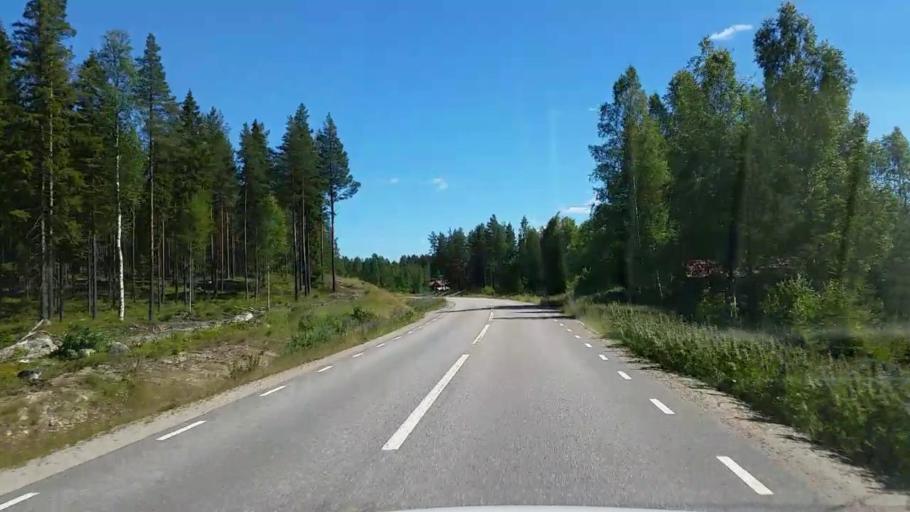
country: SE
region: Gaevleborg
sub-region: Ovanakers Kommun
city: Edsbyn
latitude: 61.4254
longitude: 15.7264
